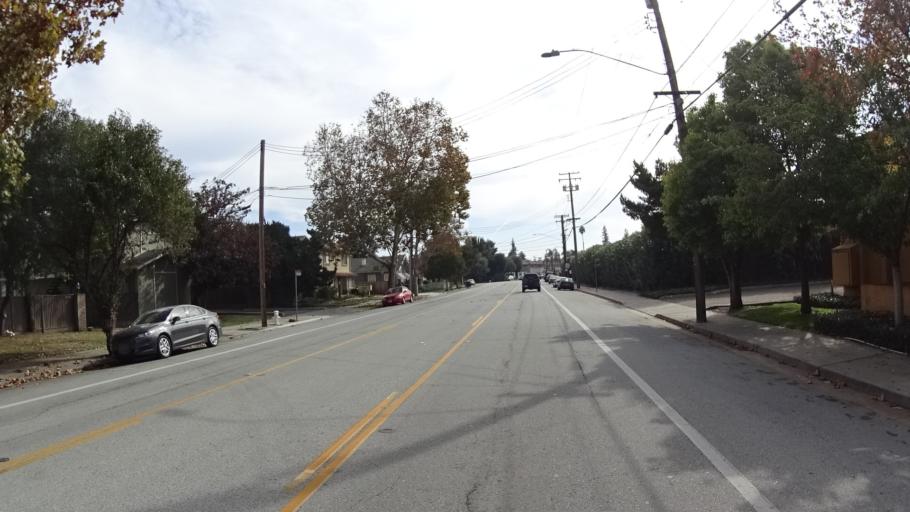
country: US
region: California
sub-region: Santa Clara County
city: Santa Clara
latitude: 37.3415
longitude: -121.9443
